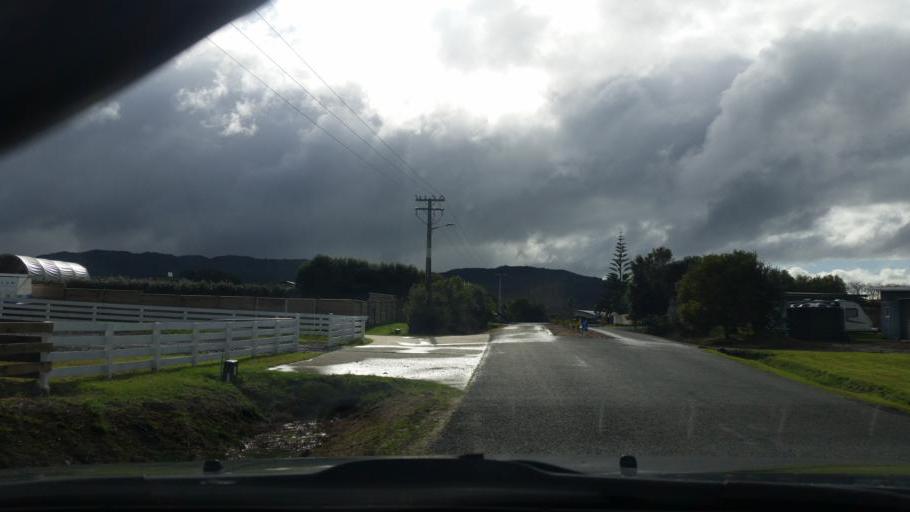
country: NZ
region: Auckland
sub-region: Auckland
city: Wellsford
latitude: -36.0922
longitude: 174.5736
